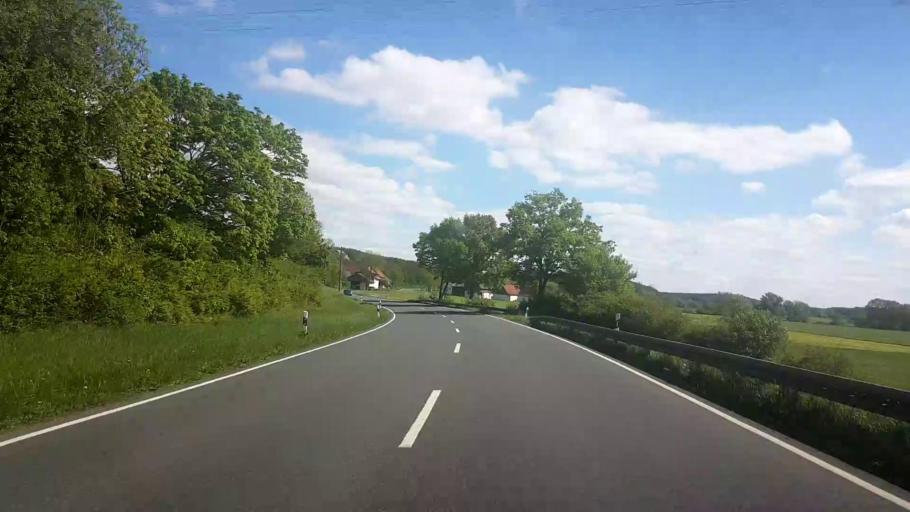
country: DE
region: Bavaria
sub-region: Upper Franconia
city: Rattelsdorf
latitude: 50.0649
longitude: 10.8708
